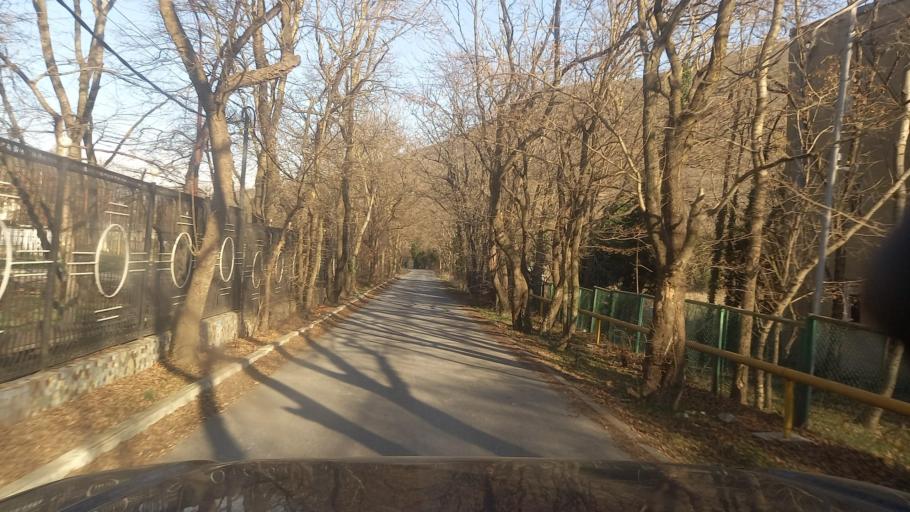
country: RU
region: Krasnodarskiy
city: Myskhako
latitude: 44.6665
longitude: 37.6854
